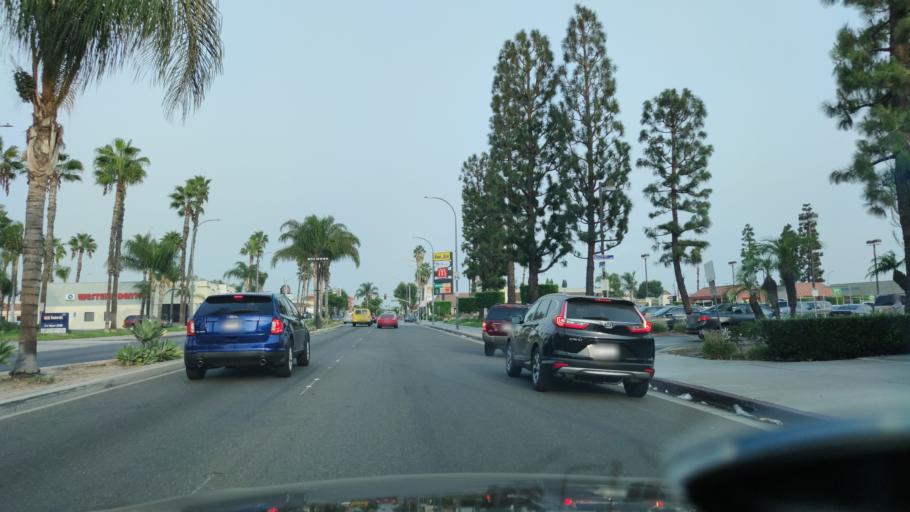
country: US
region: California
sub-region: Los Angeles County
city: Maywood
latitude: 33.9873
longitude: -118.1873
